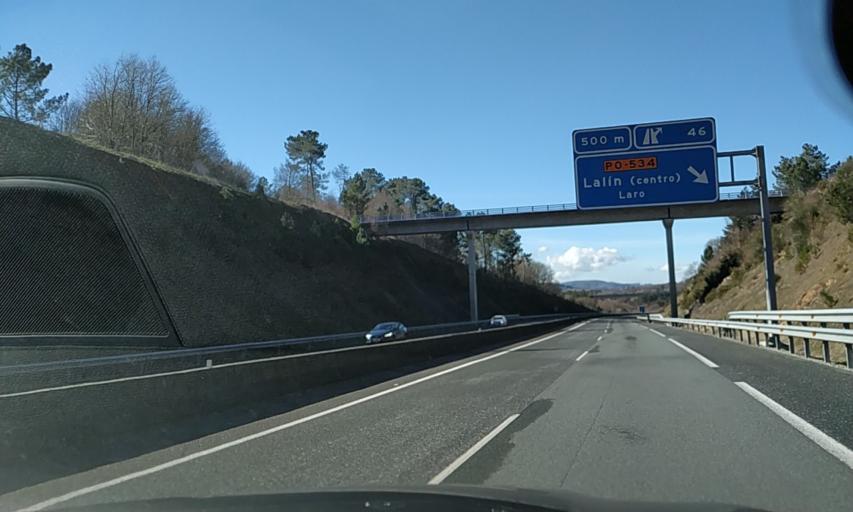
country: ES
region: Galicia
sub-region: Provincia de Pontevedra
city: Lalin
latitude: 42.6318
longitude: -8.1231
